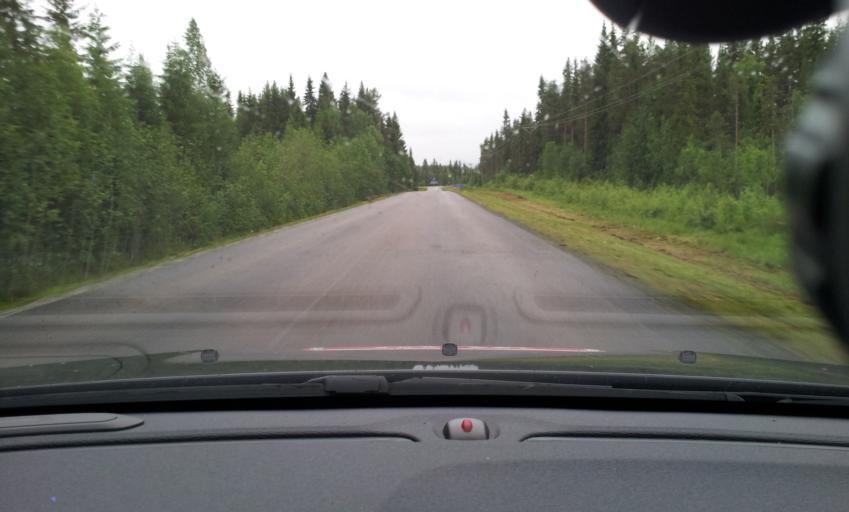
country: SE
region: Jaemtland
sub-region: Ragunda Kommun
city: Hammarstrand
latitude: 63.1844
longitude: 15.9384
